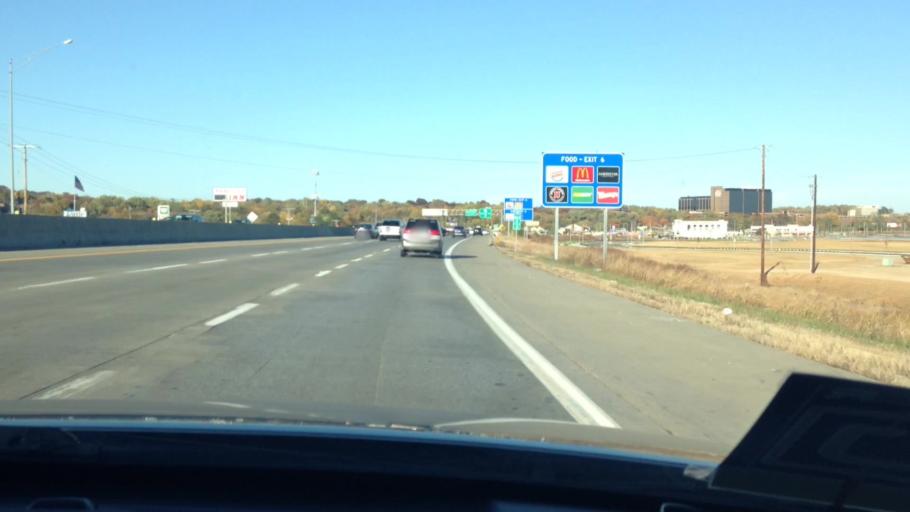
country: US
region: Missouri
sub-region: Clay County
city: North Kansas City
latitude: 39.1392
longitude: -94.5666
